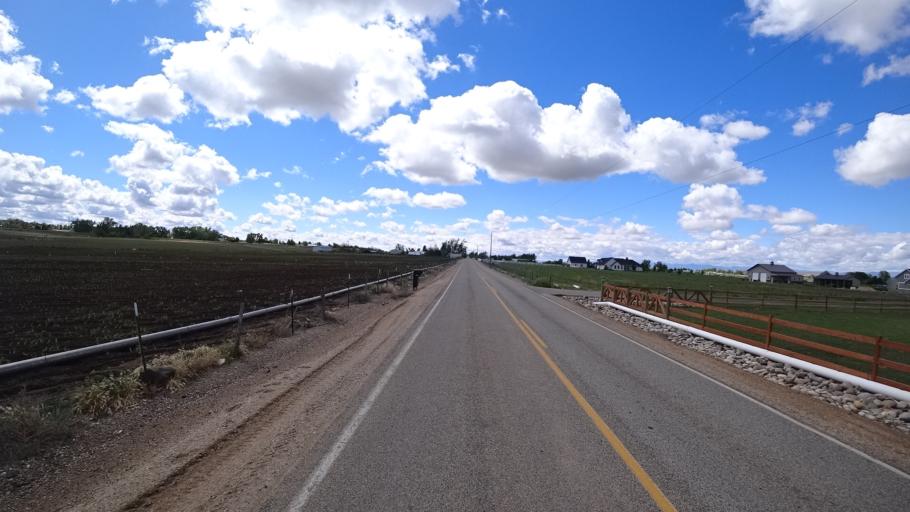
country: US
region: Idaho
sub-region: Ada County
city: Kuna
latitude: 43.5096
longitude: -116.3445
